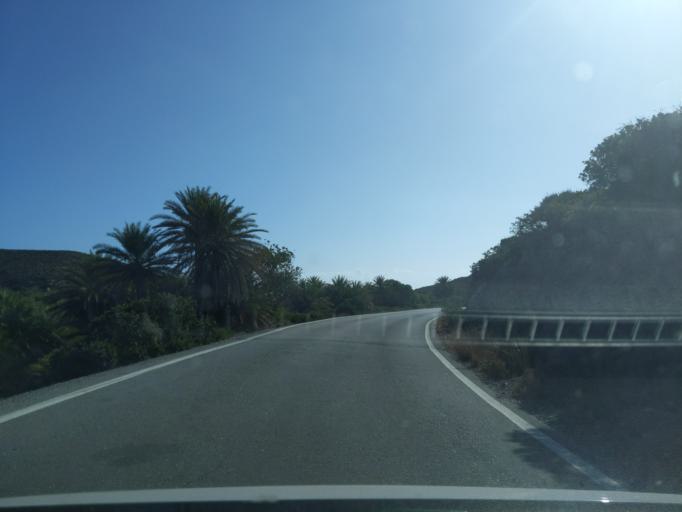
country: GR
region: Crete
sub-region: Nomos Lasithiou
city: Palekastro
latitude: 35.2548
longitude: 26.2590
